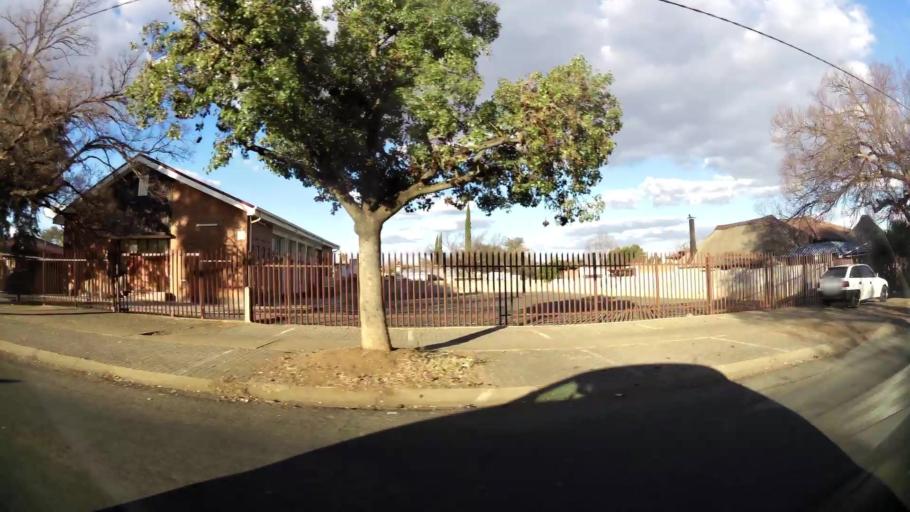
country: ZA
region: North-West
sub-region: Dr Kenneth Kaunda District Municipality
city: Potchefstroom
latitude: -26.7287
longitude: 27.0897
